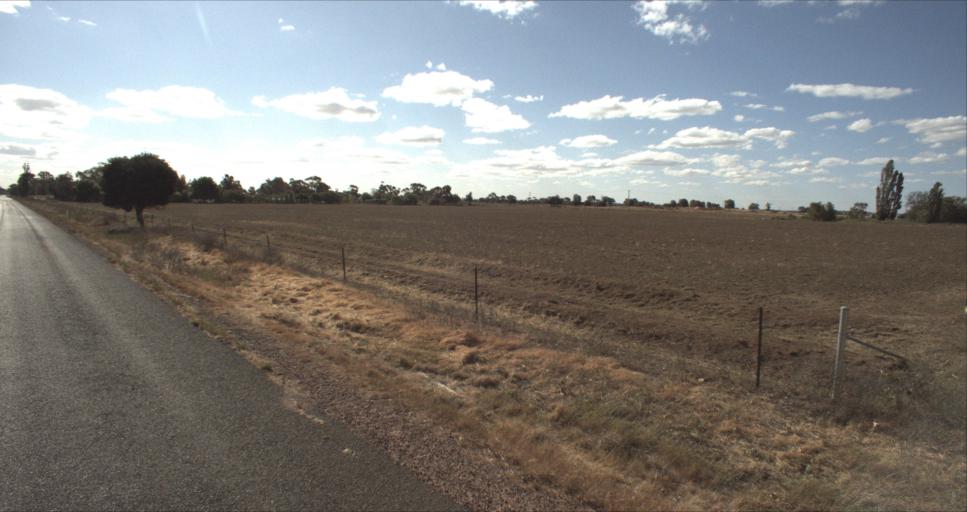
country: AU
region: New South Wales
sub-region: Griffith
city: Griffith
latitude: -34.4389
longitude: 146.2131
